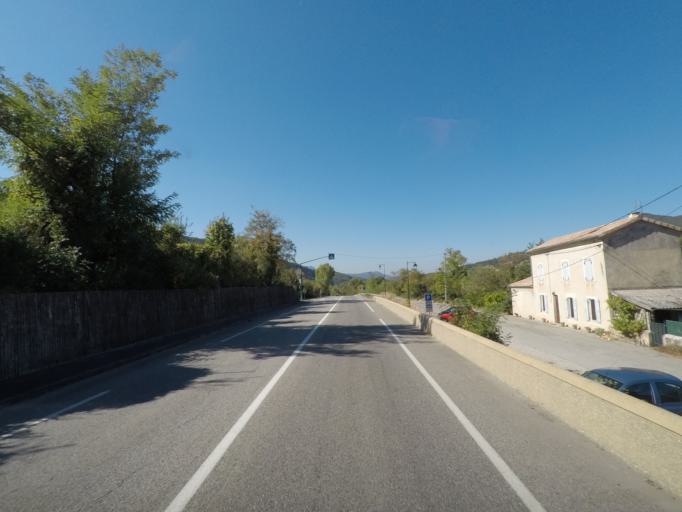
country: FR
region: Rhone-Alpes
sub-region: Departement de la Drome
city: Aouste-sur-Sye
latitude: 44.6947
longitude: 5.1942
